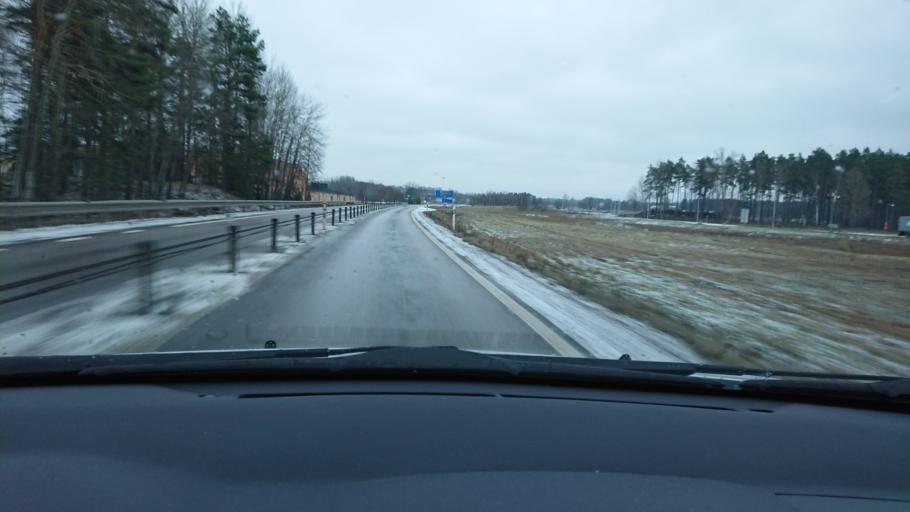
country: SE
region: Kalmar
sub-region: Vimmerby Kommun
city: Vimmerby
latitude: 57.6542
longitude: 15.8544
